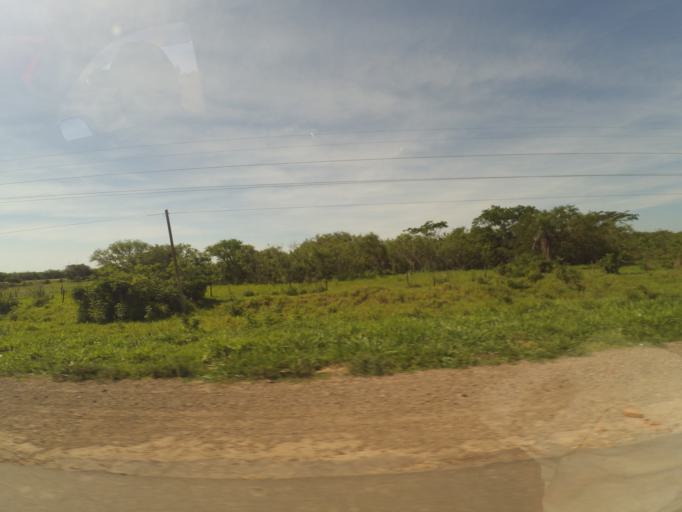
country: BO
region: Santa Cruz
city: San Julian
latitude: -17.7247
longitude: -62.9140
